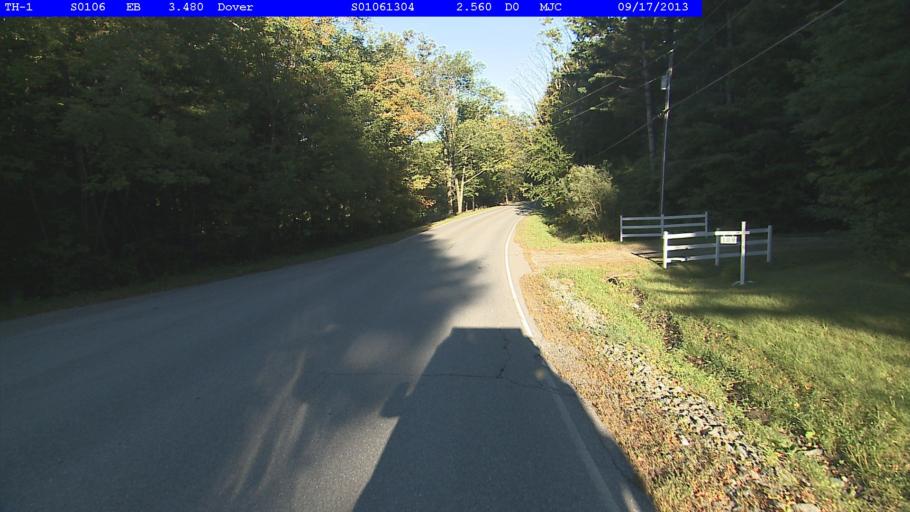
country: US
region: Vermont
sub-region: Windham County
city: Dover
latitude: 42.9461
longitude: -72.7960
